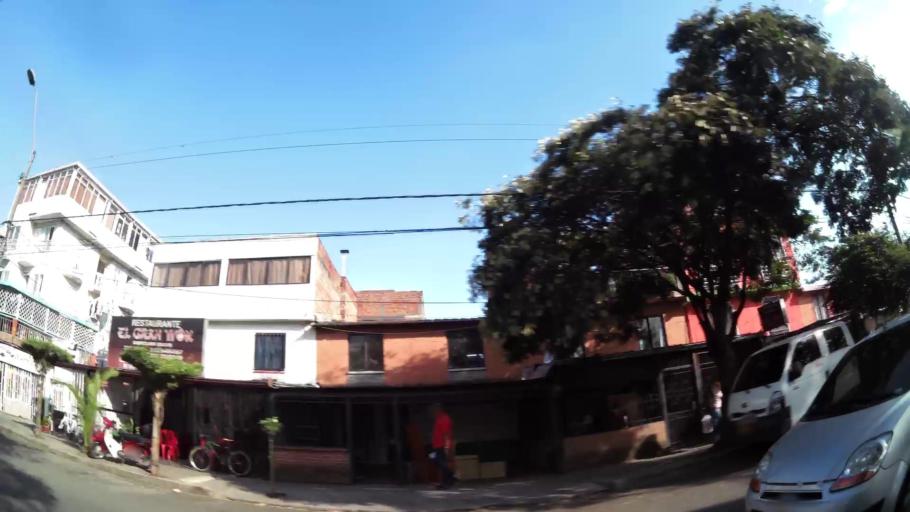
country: CO
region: Valle del Cauca
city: Cali
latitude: 3.3996
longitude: -76.5067
